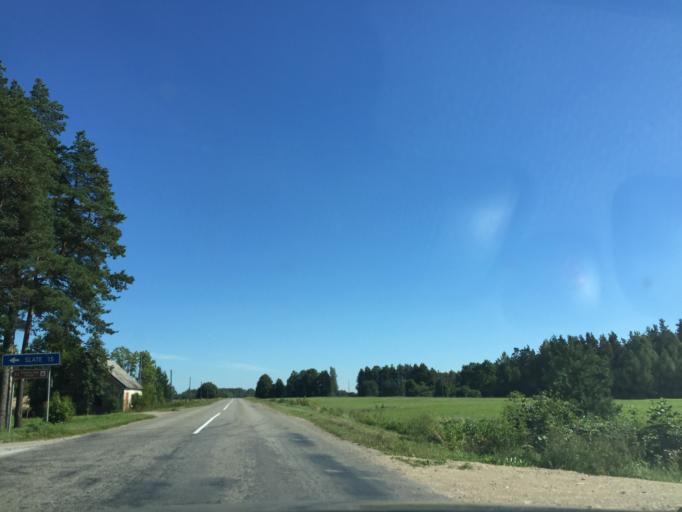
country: LV
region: Akniste
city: Akniste
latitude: 56.1462
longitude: 25.7932
